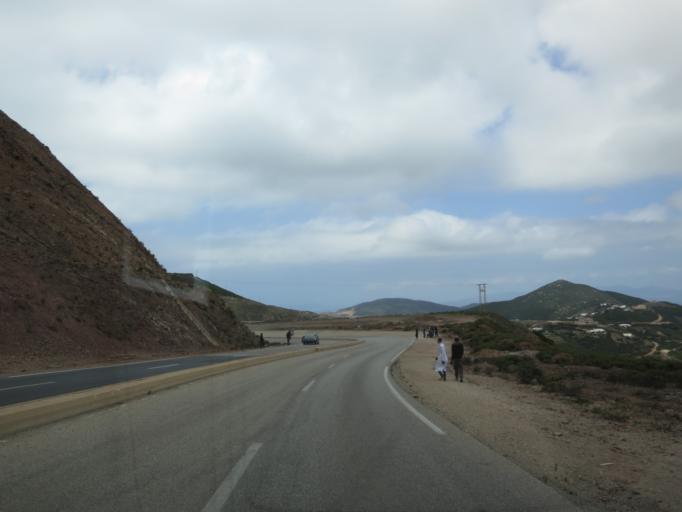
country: ES
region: Ceuta
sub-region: Ceuta
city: Ceuta
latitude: 35.8547
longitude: -5.4392
